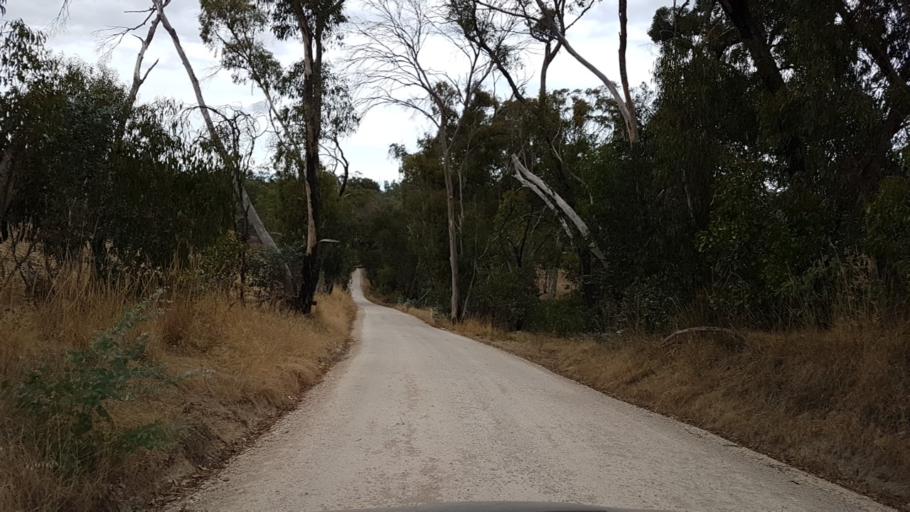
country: AU
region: South Australia
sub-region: Adelaide Hills
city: Gumeracha
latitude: -34.7989
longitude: 138.8340
